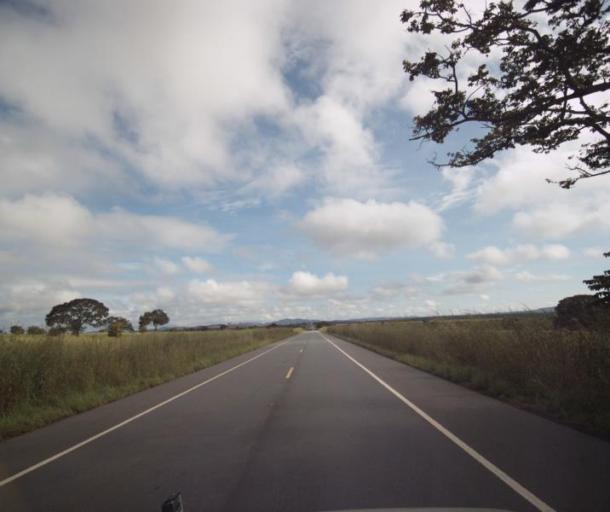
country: BR
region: Goias
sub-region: Barro Alto
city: Barro Alto
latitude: -15.2424
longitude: -48.6908
